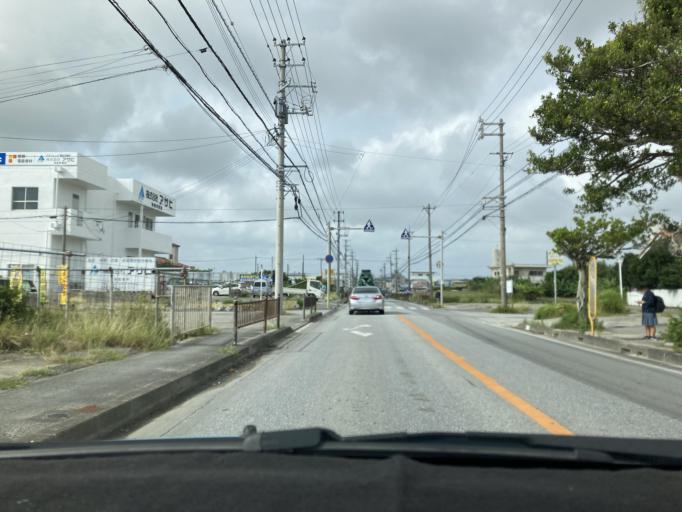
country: JP
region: Okinawa
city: Tomigusuku
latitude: 26.1657
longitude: 127.6684
